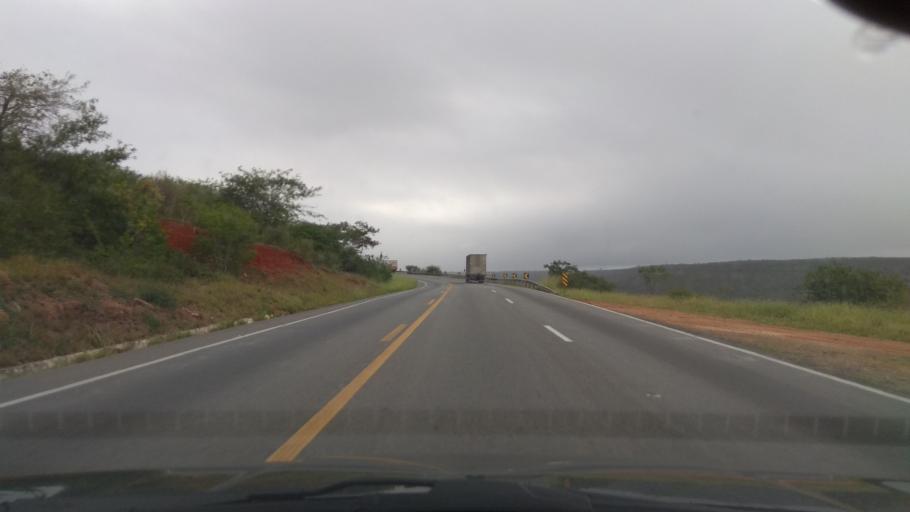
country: BR
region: Bahia
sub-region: Santa Ines
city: Santa Ines
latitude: -13.0371
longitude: -39.9673
